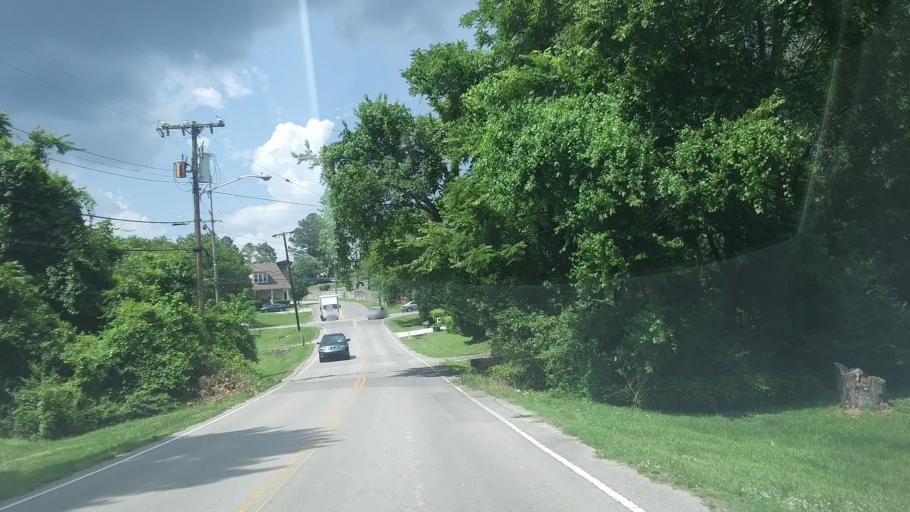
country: US
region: Tennessee
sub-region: Davidson County
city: Oak Hill
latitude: 36.0786
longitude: -86.7146
